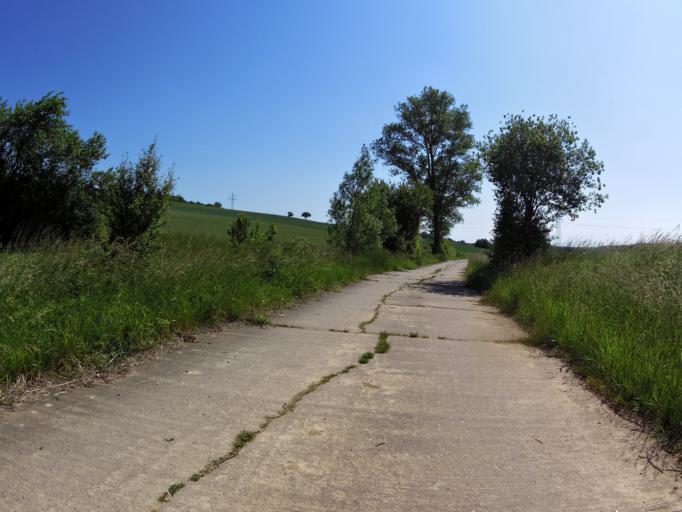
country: DE
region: Bavaria
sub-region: Regierungsbezirk Unterfranken
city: Kleinrinderfeld
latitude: 49.7068
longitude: 9.8542
